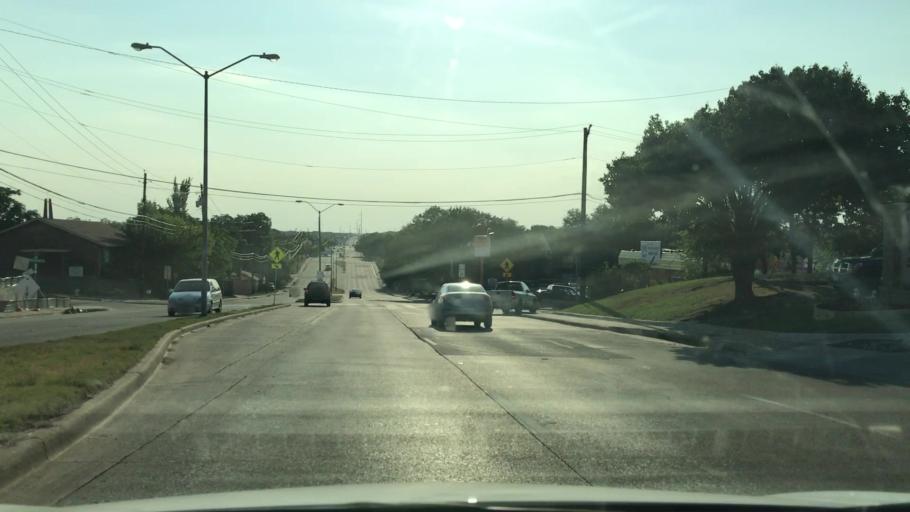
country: US
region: Texas
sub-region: Dallas County
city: Cockrell Hill
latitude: 32.7496
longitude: -96.8507
